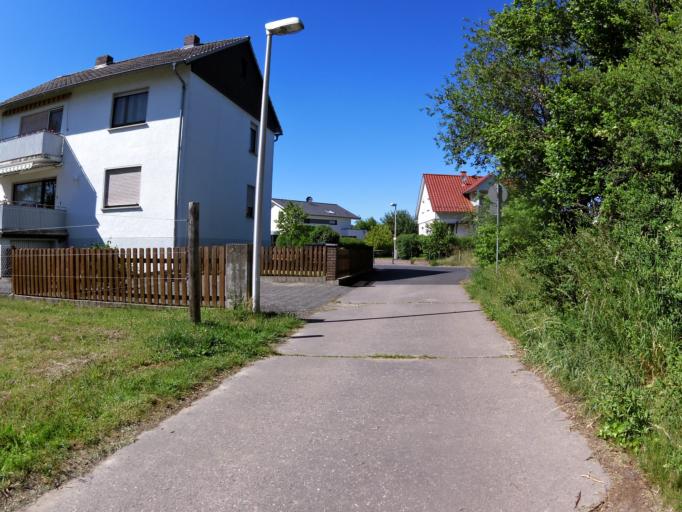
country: DE
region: Thuringia
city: Dippach
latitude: 50.9469
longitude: 10.0437
